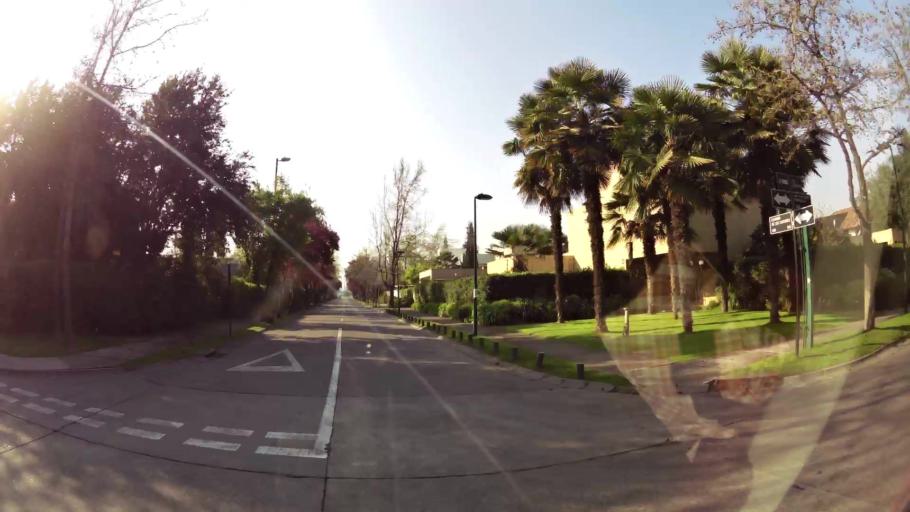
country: CL
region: Santiago Metropolitan
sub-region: Provincia de Santiago
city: Villa Presidente Frei, Nunoa, Santiago, Chile
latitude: -33.3639
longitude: -70.5381
